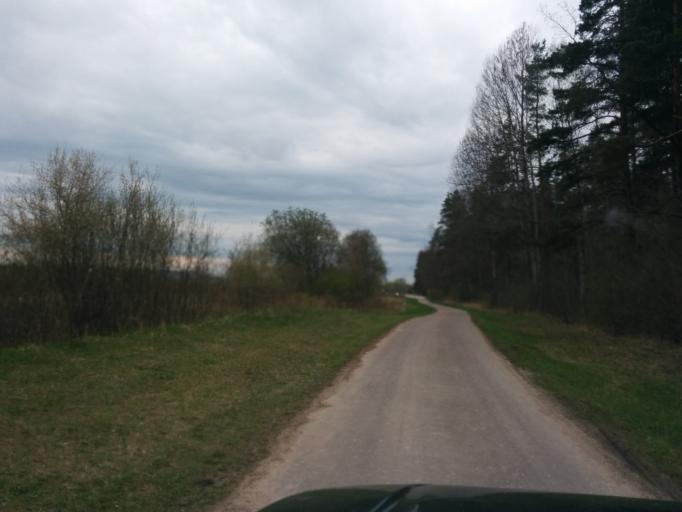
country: LV
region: Ozolnieku
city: Ozolnieki
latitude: 56.6708
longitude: 23.7758
